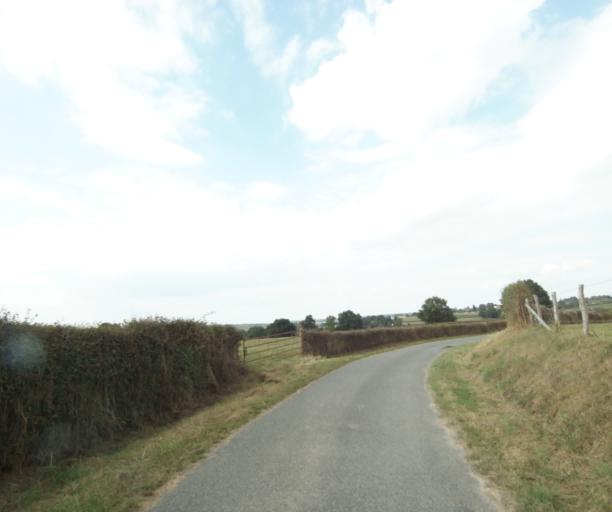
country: FR
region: Bourgogne
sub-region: Departement de Saone-et-Loire
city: Palinges
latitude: 46.4858
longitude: 4.1953
